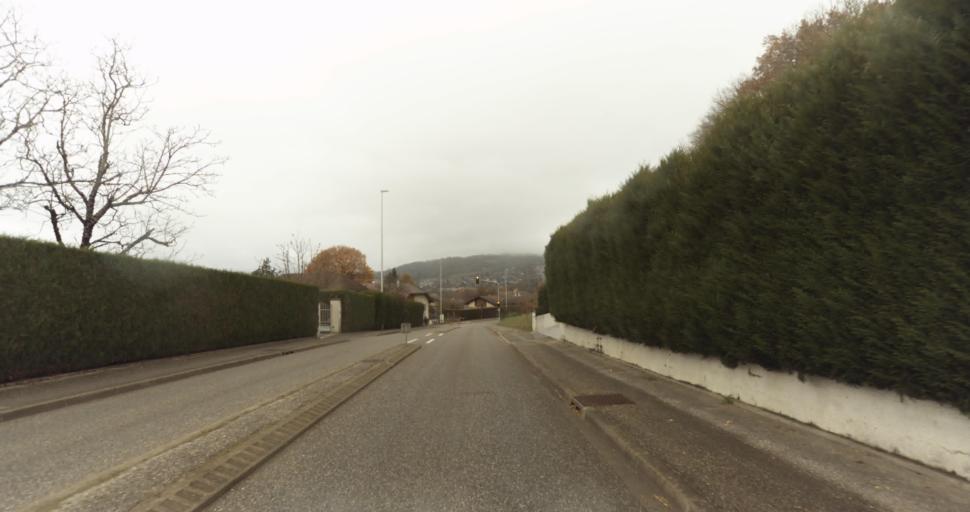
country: FR
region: Rhone-Alpes
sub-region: Departement de la Haute-Savoie
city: Annecy-le-Vieux
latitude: 45.9283
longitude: 6.1395
